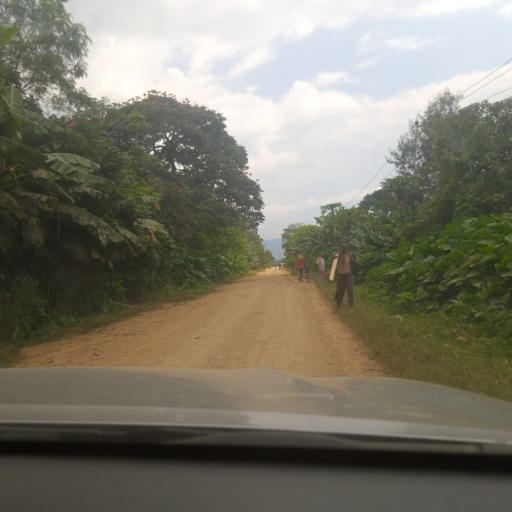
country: ET
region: Southern Nations, Nationalities, and People's Region
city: Tippi
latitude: 7.1353
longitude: 35.4239
